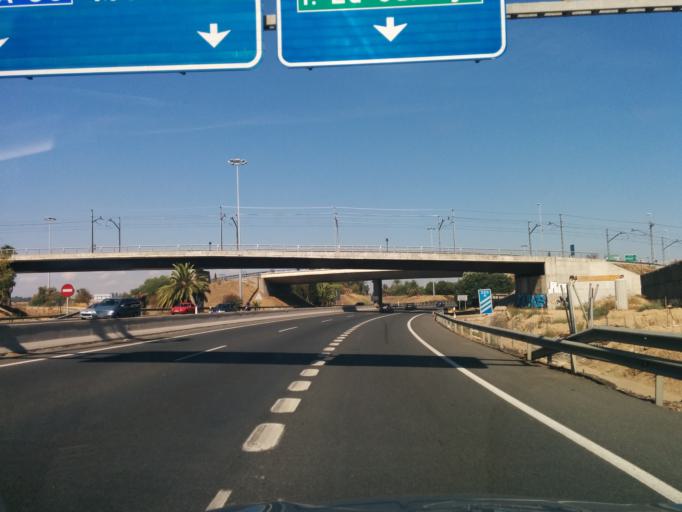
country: ES
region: Andalusia
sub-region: Provincia de Sevilla
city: San Juan de Aznalfarache
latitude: 37.3674
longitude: -6.0141
